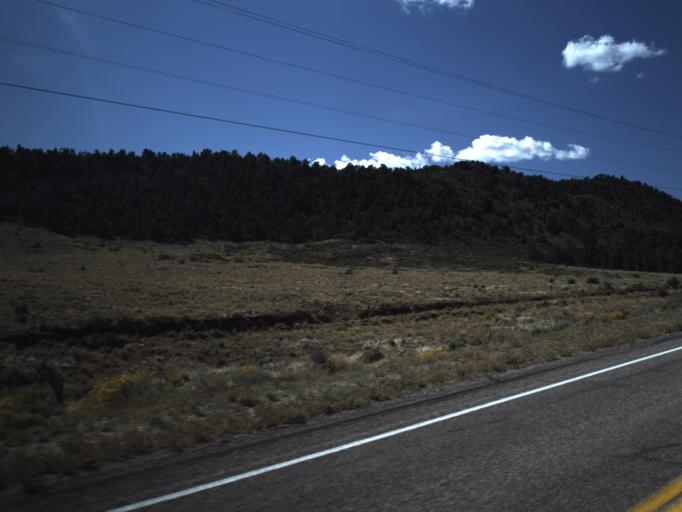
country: US
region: Utah
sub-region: Iron County
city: Cedar City
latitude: 37.6219
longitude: -113.3243
